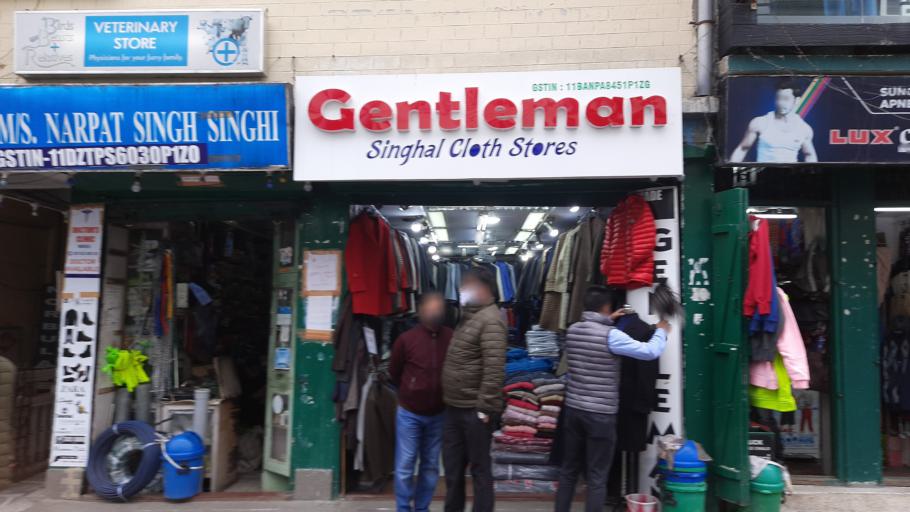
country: IN
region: Sikkim
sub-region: East District
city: Gangtok
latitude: 27.3288
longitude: 88.6124
